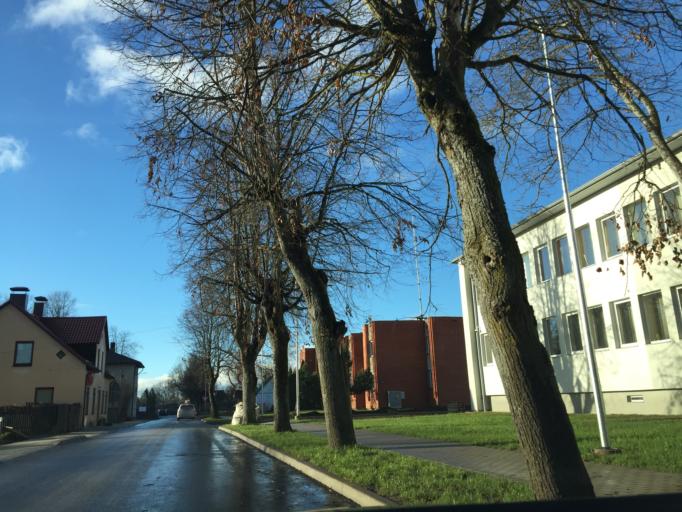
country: LV
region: Valmieras Rajons
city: Valmiera
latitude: 57.5362
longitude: 25.4151
